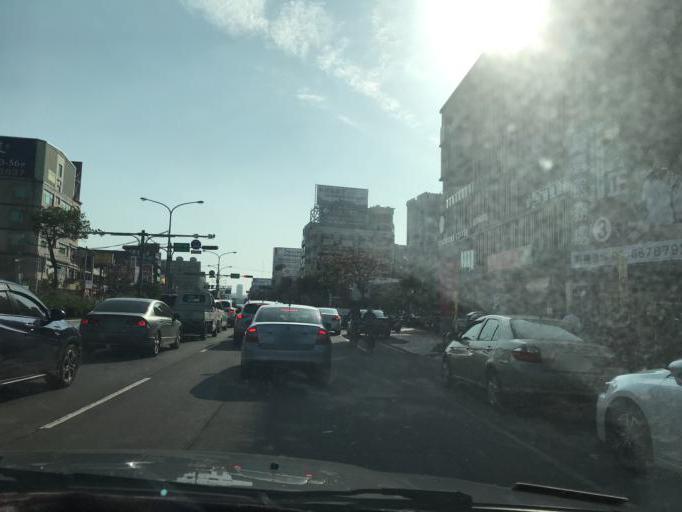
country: TW
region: Taiwan
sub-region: Hsinchu
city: Zhubei
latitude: 24.8158
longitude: 121.0249
